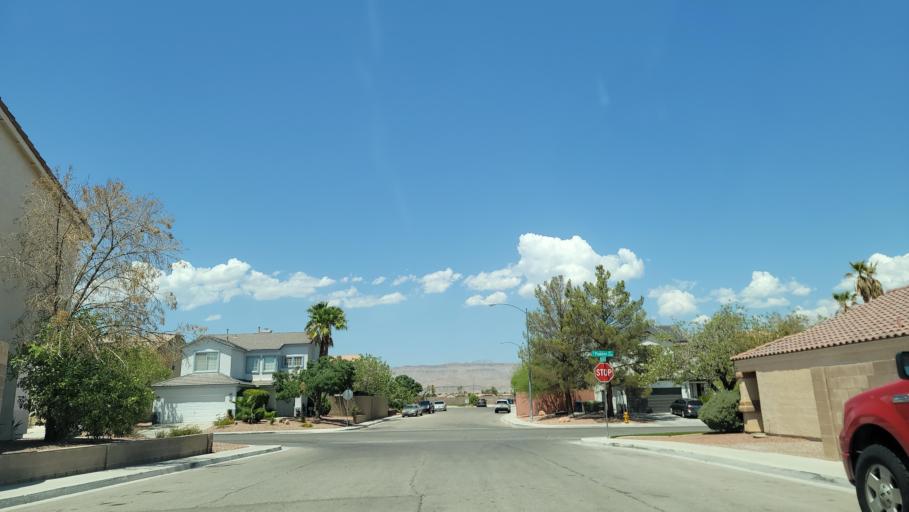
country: US
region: Nevada
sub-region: Clark County
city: Spring Valley
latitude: 36.0838
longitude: -115.2559
